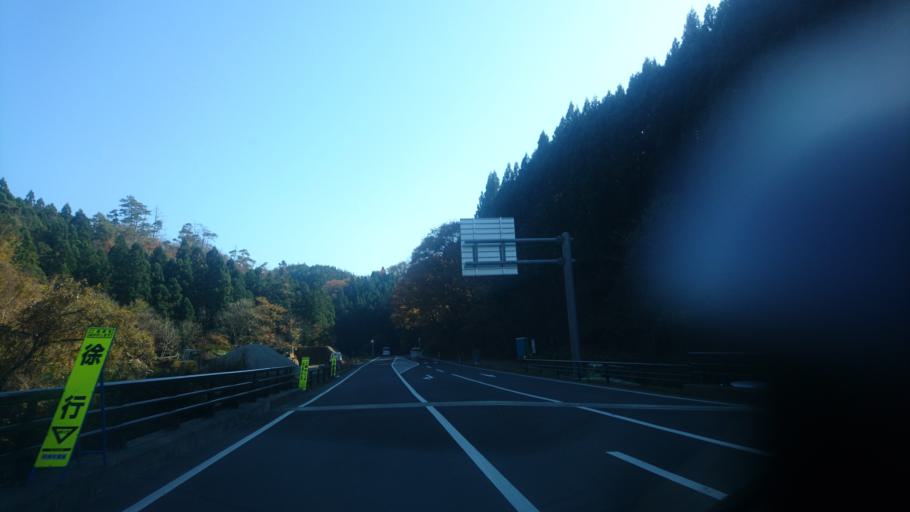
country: JP
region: Miyagi
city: Okawara
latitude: 38.1315
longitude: 140.7586
